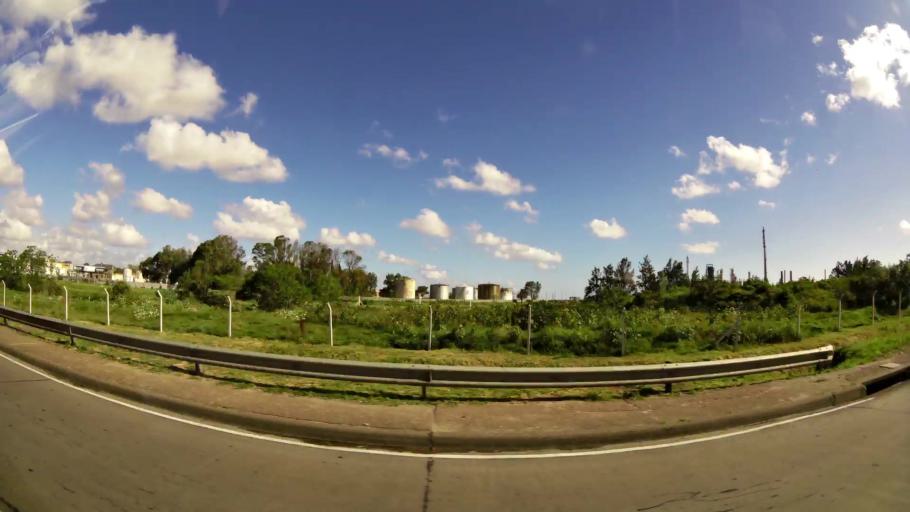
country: UY
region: Montevideo
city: Montevideo
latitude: -34.8688
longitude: -56.2244
